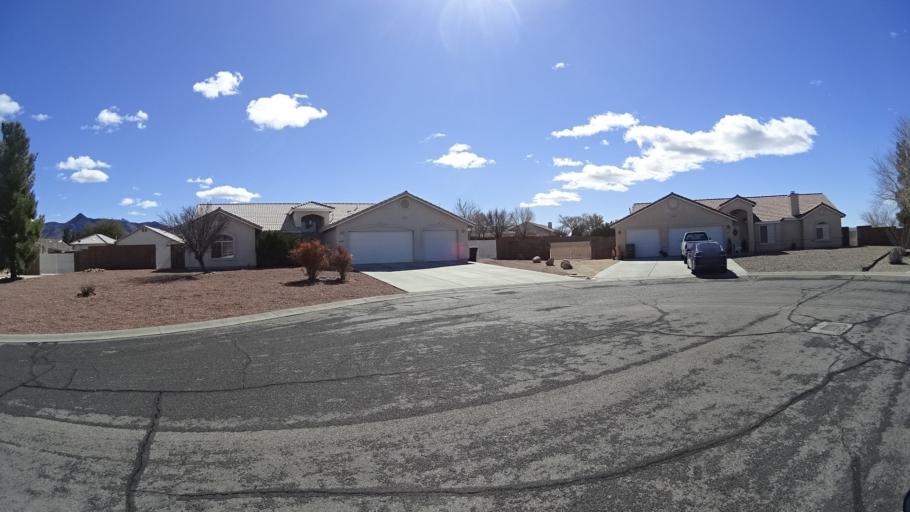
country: US
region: Arizona
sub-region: Mohave County
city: Kingman
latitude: 35.2062
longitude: -113.9755
